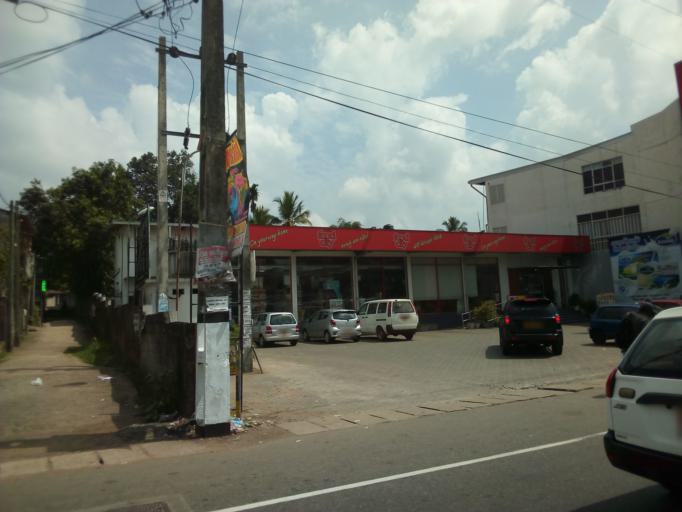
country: LK
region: Western
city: Maharagama
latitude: 6.8422
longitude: 79.9621
